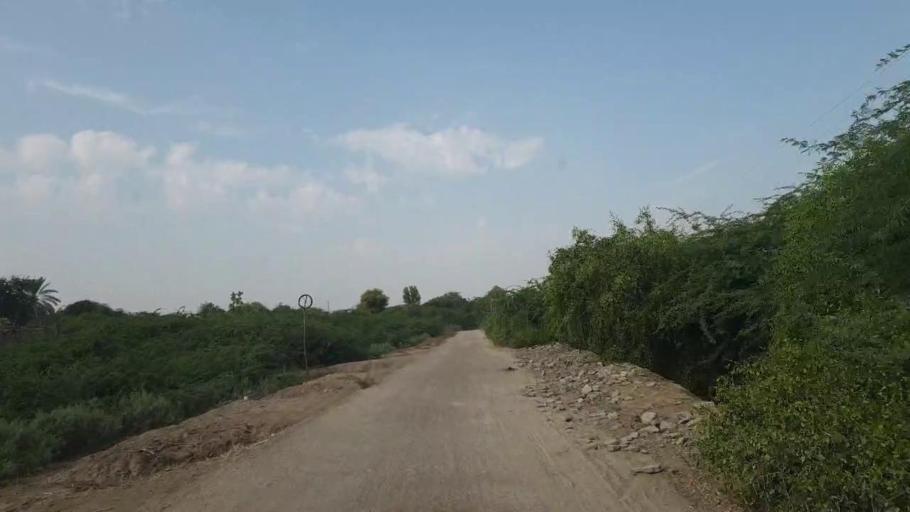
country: PK
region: Sindh
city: Digri
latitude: 25.0084
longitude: 69.0635
